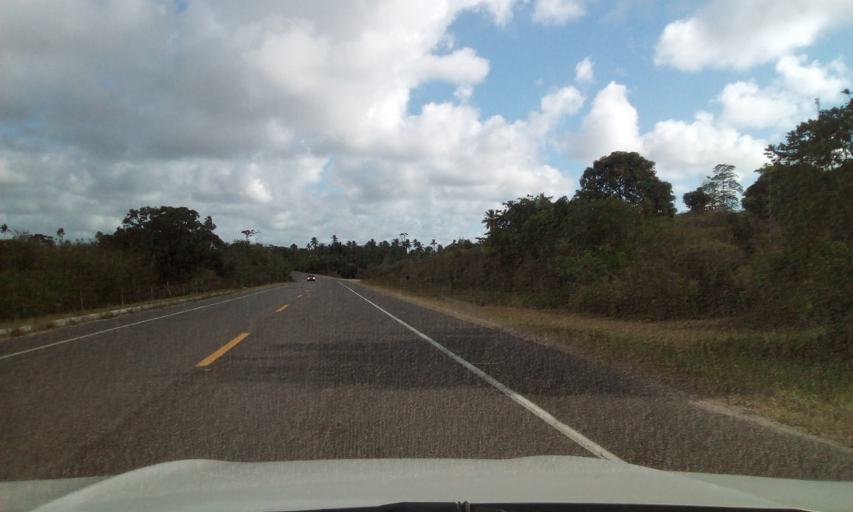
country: BR
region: Bahia
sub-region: Conde
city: Conde
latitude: -11.8015
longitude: -37.6283
